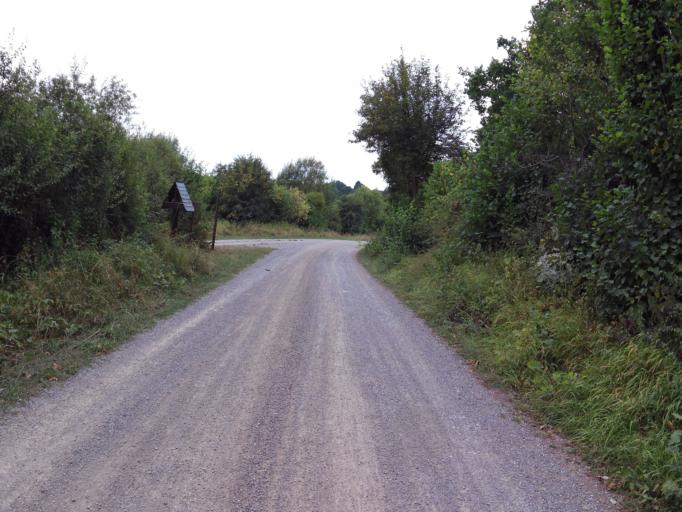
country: DE
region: North Rhine-Westphalia
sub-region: Regierungsbezirk Koln
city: Nettersheim
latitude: 50.5041
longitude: 6.6234
